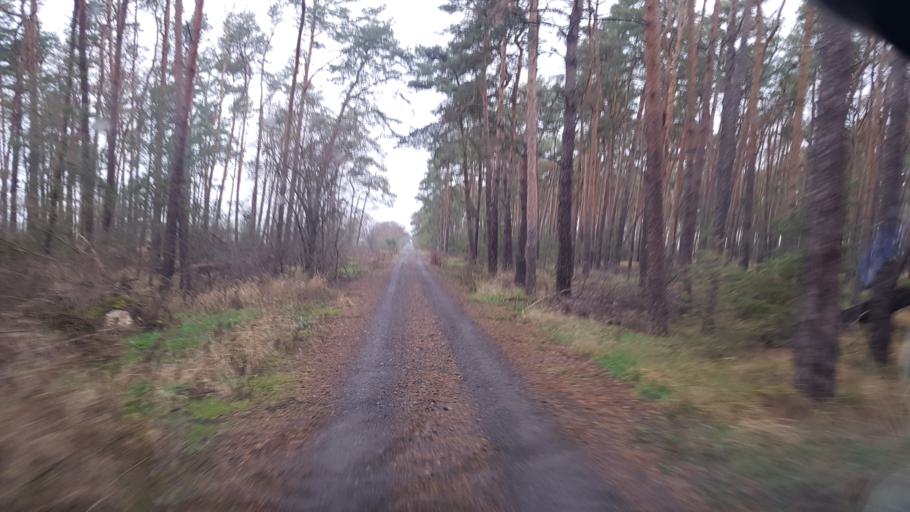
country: DE
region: Brandenburg
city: Muhlberg
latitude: 51.4974
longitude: 13.2951
